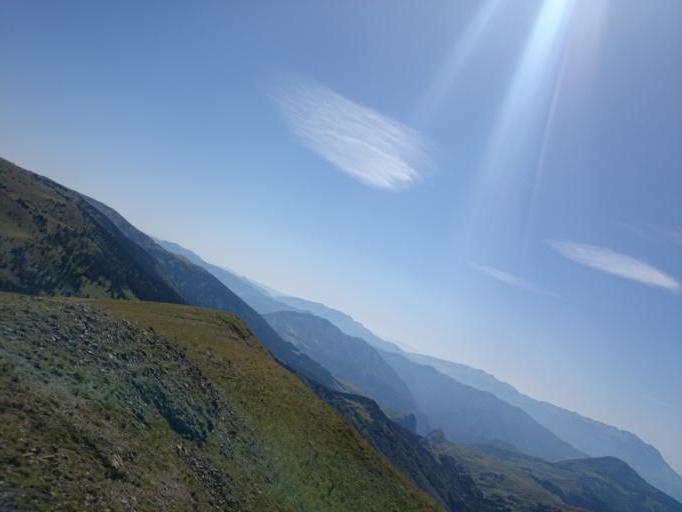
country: AL
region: Elbasan
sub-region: Rrethi i Gramshit
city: Lenias
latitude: 40.8300
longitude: 20.4497
